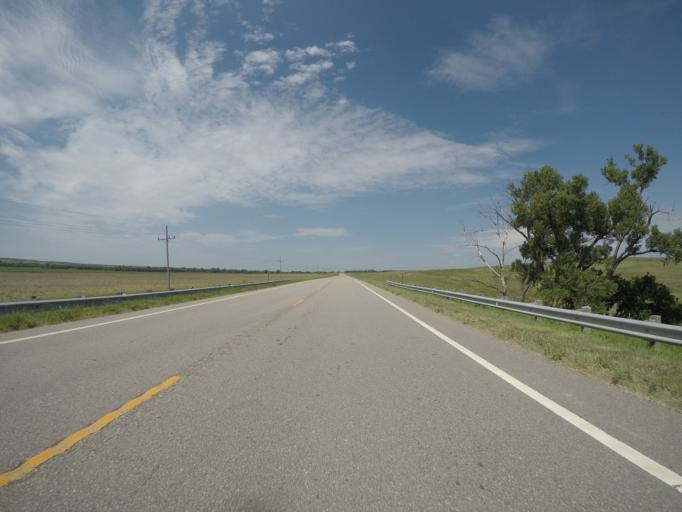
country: US
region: Kansas
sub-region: Rooks County
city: Stockton
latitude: 39.4445
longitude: -99.1707
